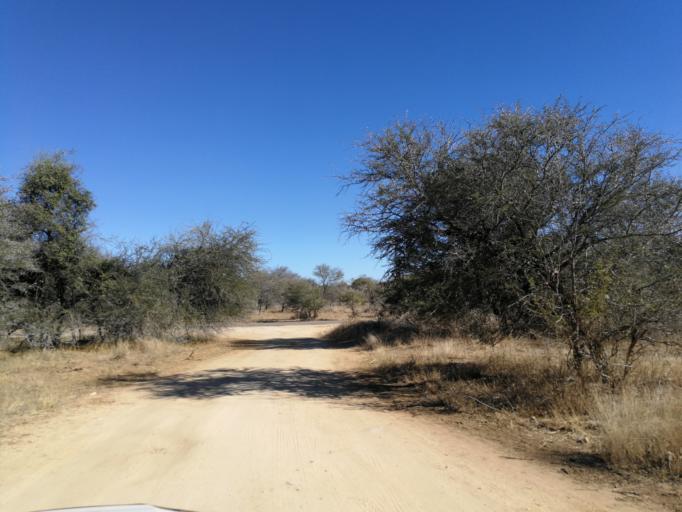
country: ZA
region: Limpopo
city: Thulamahashi
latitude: -24.9657
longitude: 31.6818
